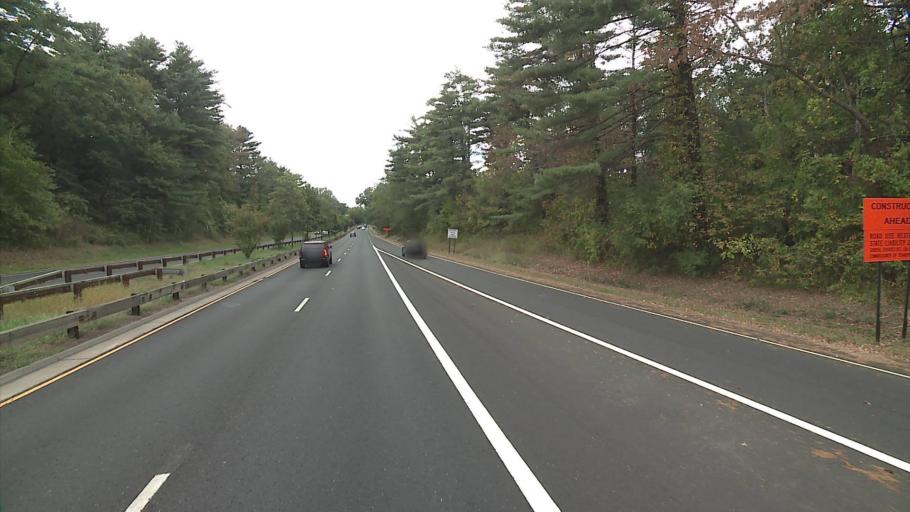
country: US
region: Connecticut
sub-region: Fairfield County
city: Glenville
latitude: 41.0940
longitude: -73.6539
